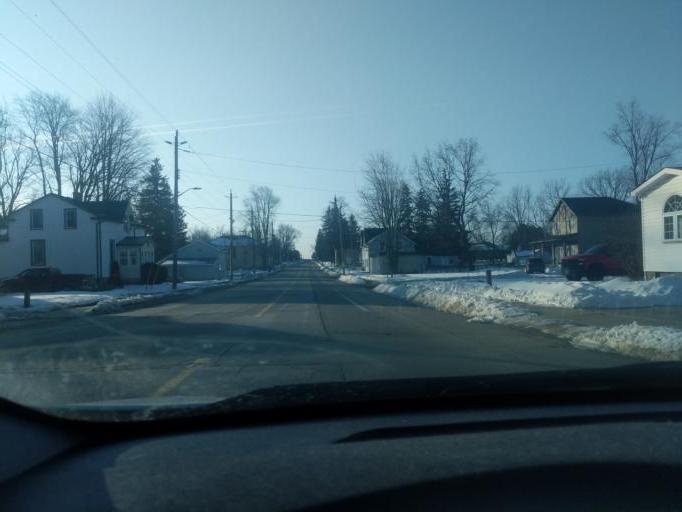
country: CA
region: Ontario
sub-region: Oxford County
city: Woodstock
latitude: 43.2709
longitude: -80.6577
